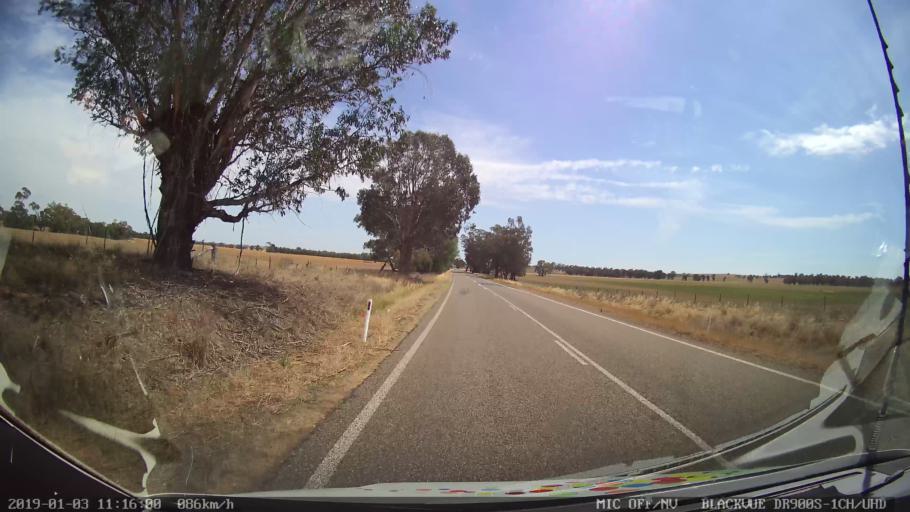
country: AU
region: New South Wales
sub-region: Young
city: Young
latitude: -34.1574
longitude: 148.2687
